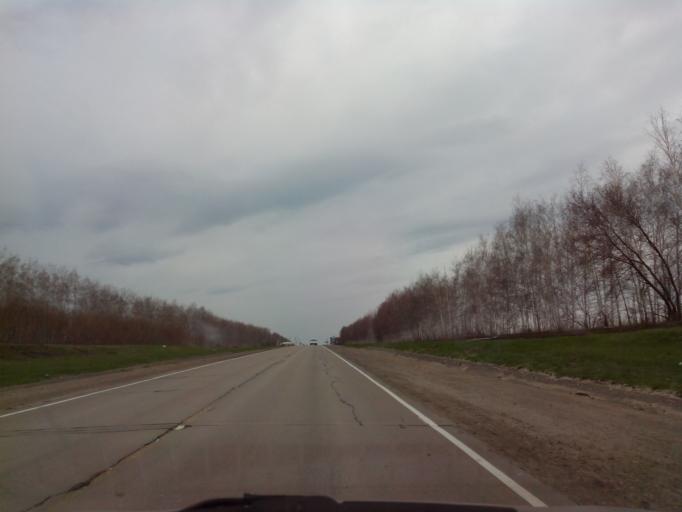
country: RU
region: Tambov
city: Znamenka
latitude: 52.3976
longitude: 41.3955
